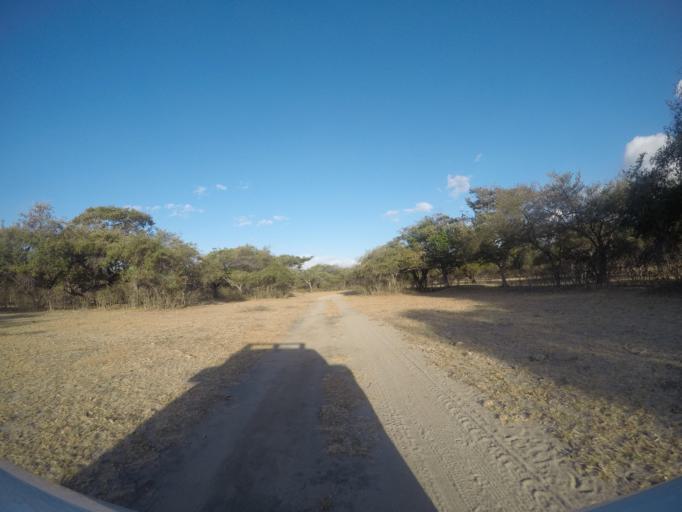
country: TL
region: Lautem
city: Lospalos
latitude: -8.3235
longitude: 127.0002
